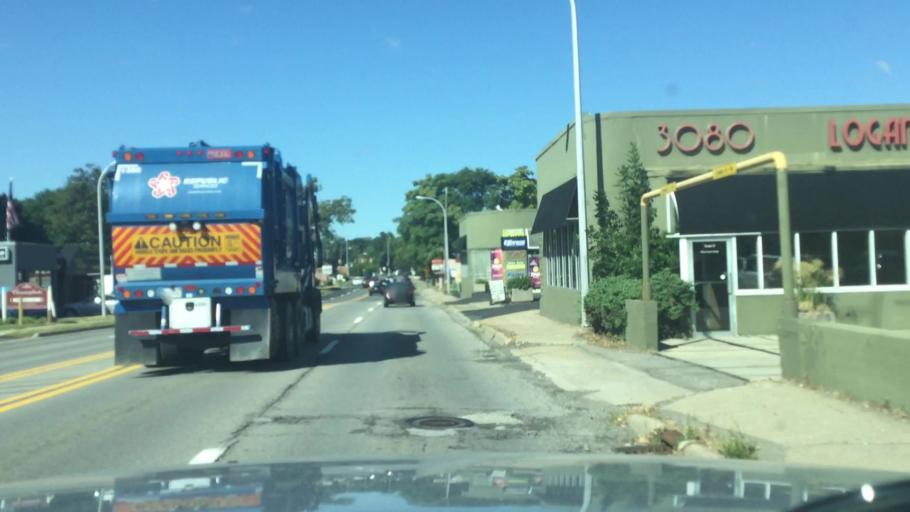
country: US
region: Michigan
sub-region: Oakland County
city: Keego Harbor
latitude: 42.6053
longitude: -83.3453
